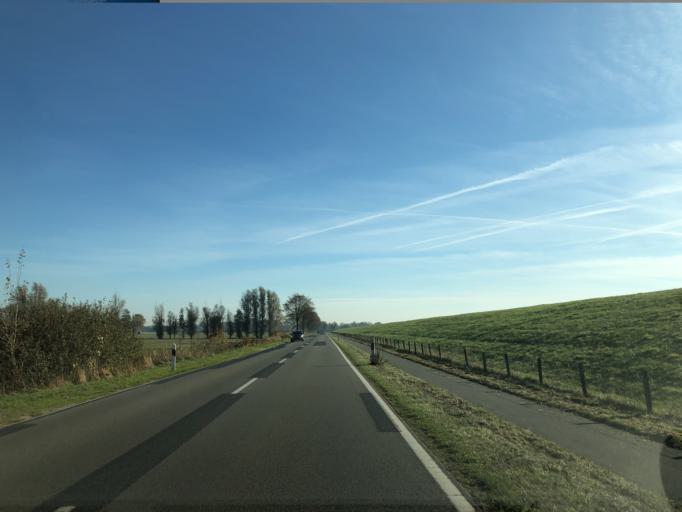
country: DE
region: Lower Saxony
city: Rhede
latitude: 53.0587
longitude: 7.3017
